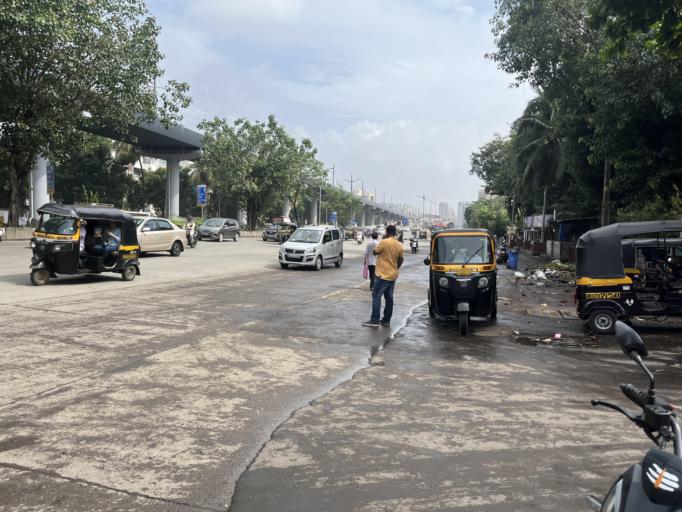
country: IN
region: Maharashtra
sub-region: Mumbai Suburban
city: Borivli
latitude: 19.2278
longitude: 72.8636
